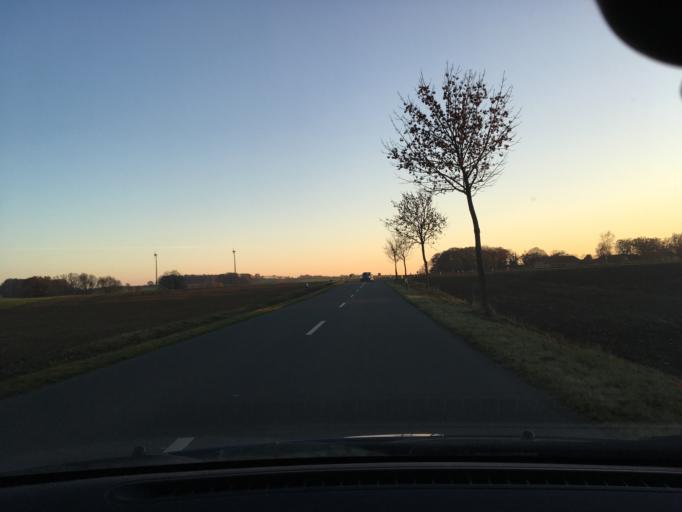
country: DE
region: Lower Saxony
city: Natendorf
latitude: 53.0628
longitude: 10.4585
